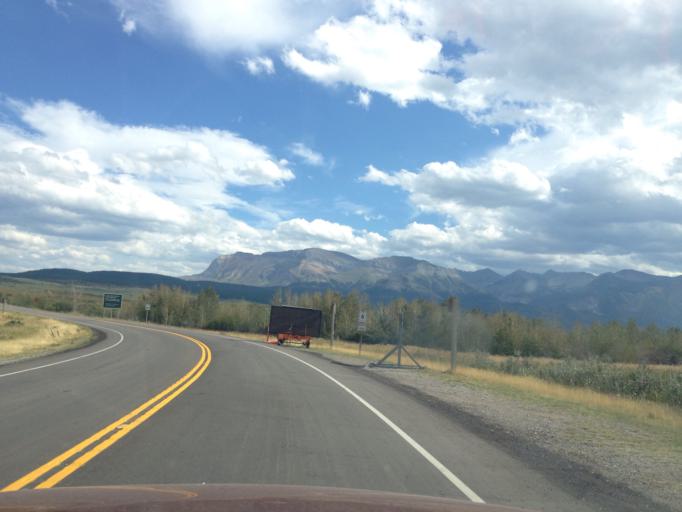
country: CA
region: Alberta
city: Pincher Creek
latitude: 49.1117
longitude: -113.8312
